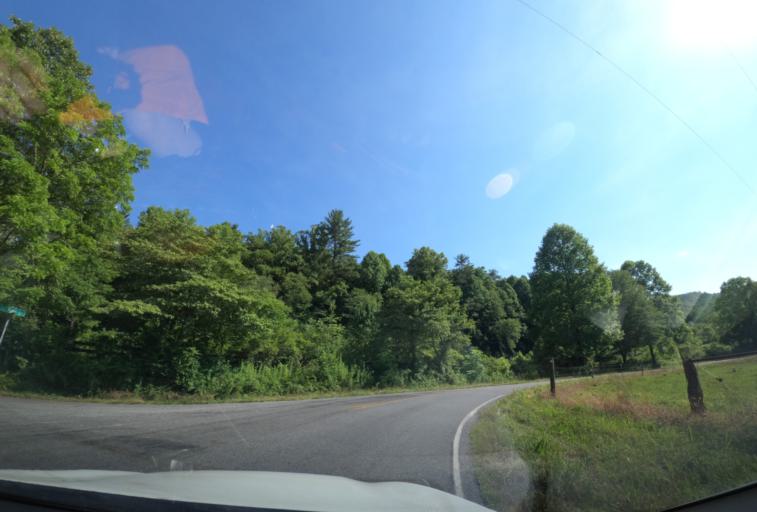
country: US
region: North Carolina
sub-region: Transylvania County
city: Brevard
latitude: 35.2260
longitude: -82.6404
